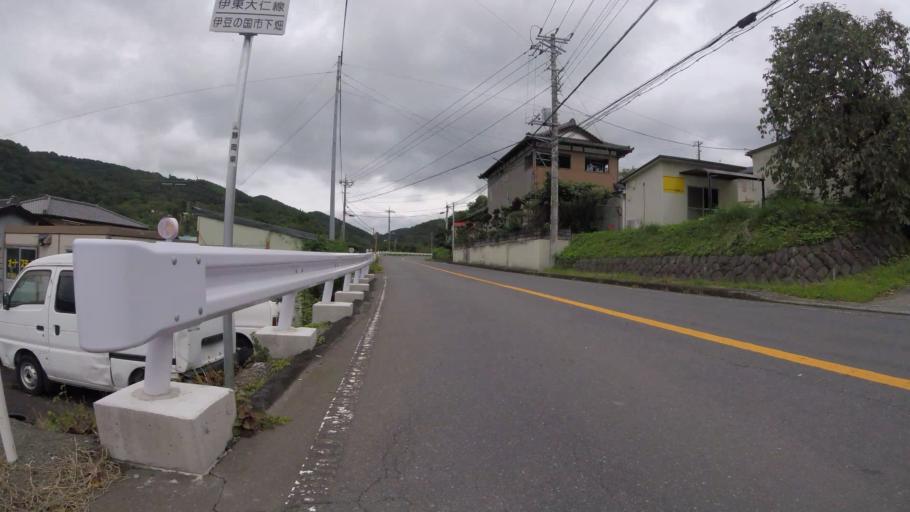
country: JP
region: Shizuoka
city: Ito
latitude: 35.0062
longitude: 138.9783
